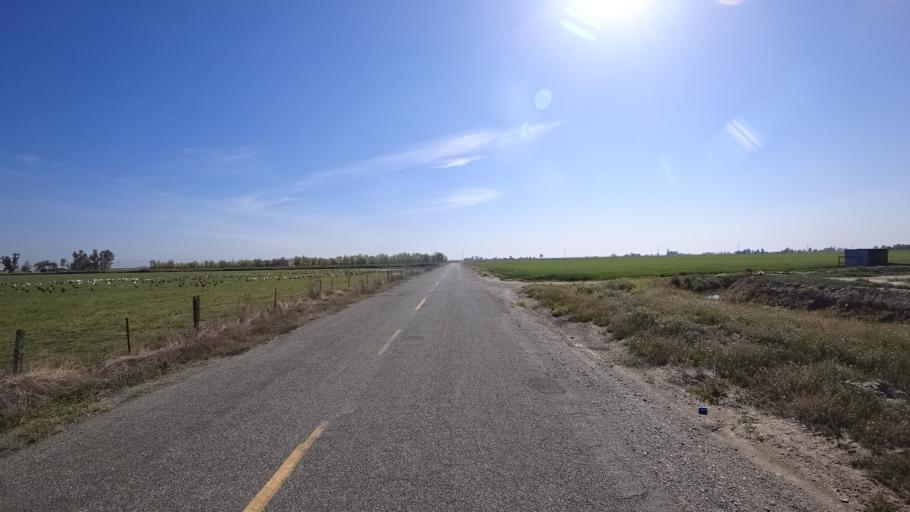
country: US
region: California
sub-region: Glenn County
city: Willows
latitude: 39.5389
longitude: -122.1409
